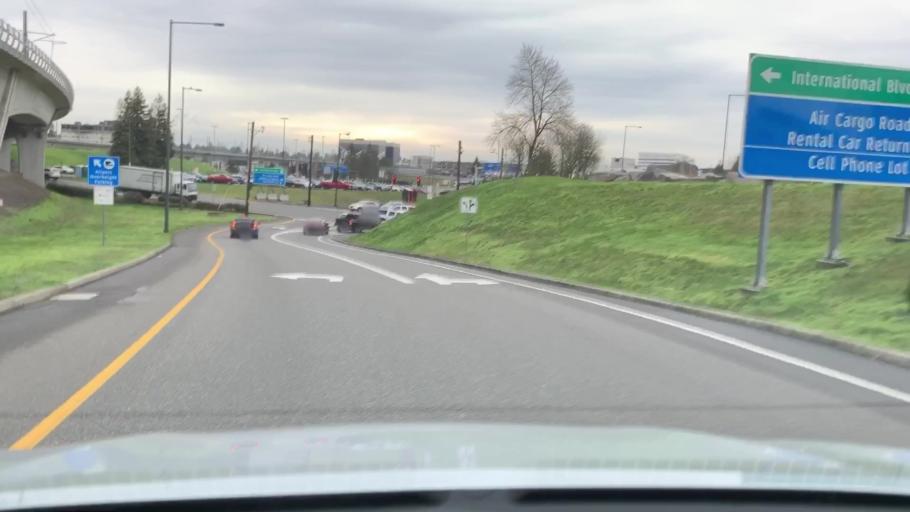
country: US
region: Washington
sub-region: King County
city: SeaTac
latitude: 47.4515
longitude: -122.3002
